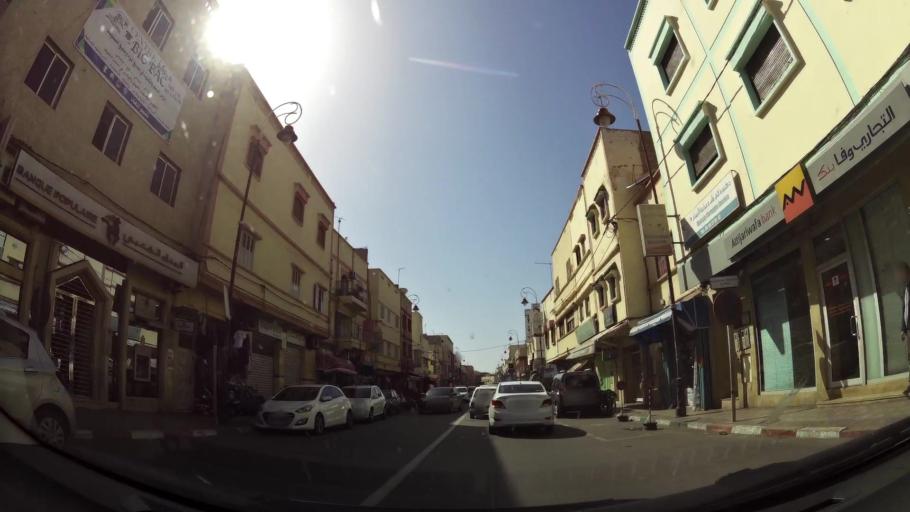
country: MA
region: Souss-Massa-Draa
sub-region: Inezgane-Ait Mellou
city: Inezgane
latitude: 30.3704
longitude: -9.5397
